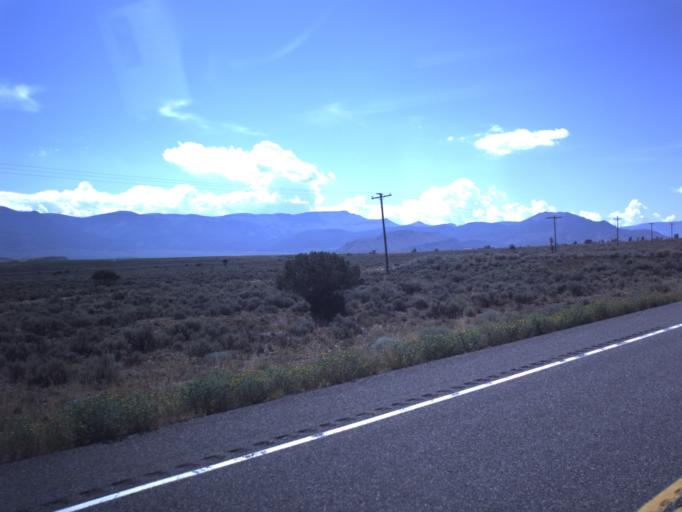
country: US
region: Utah
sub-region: Piute County
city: Junction
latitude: 38.3995
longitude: -112.2311
